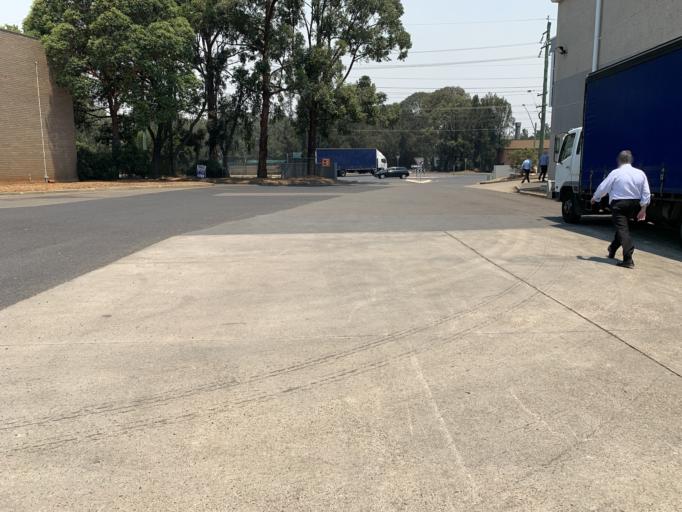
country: AU
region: New South Wales
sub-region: Holroyd
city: Girraween
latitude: -33.7743
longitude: 150.9514
